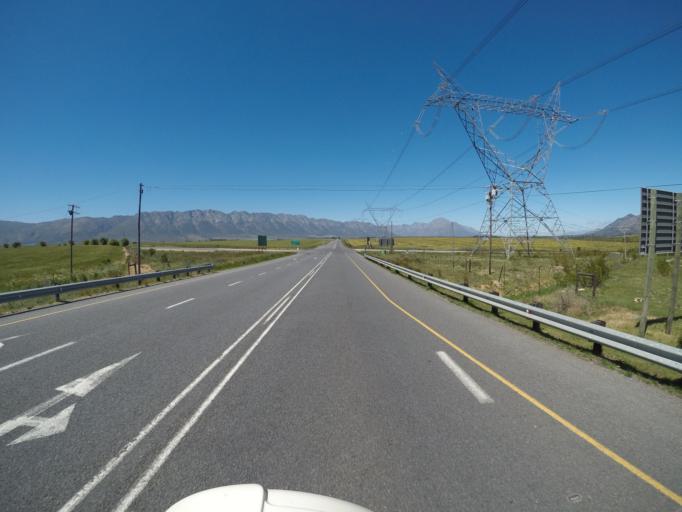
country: ZA
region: Western Cape
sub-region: Cape Winelands District Municipality
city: Ceres
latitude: -33.3087
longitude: 19.1137
